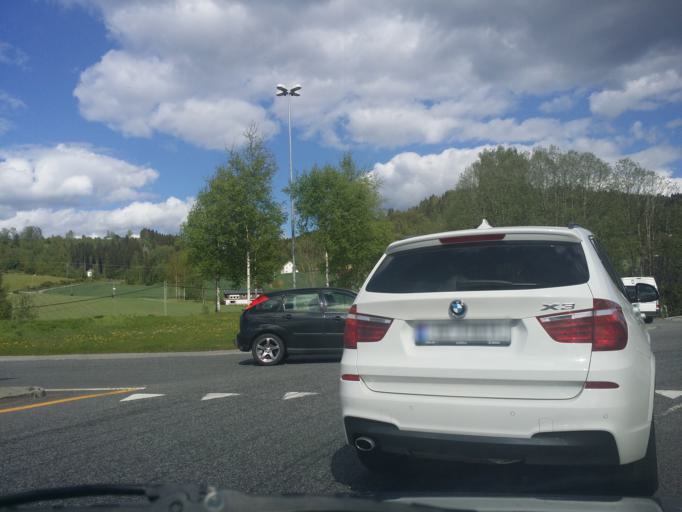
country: NO
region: Oppland
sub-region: Lunner
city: Roa
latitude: 60.2955
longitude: 10.6090
